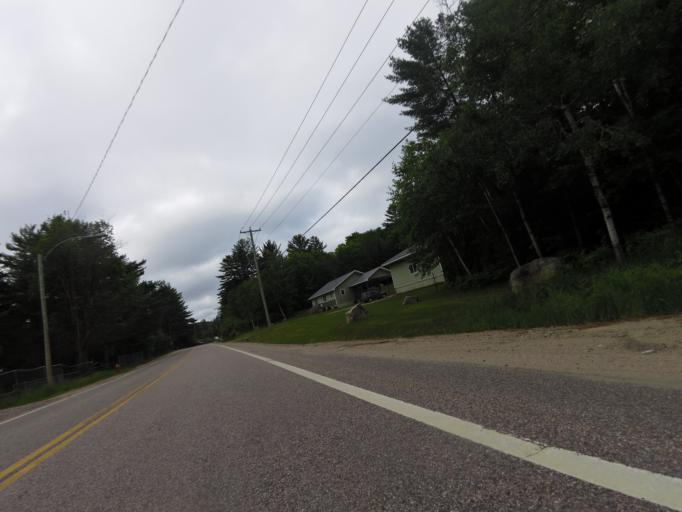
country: CA
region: Quebec
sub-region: Outaouais
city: Shawville
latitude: 45.8574
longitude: -76.4263
